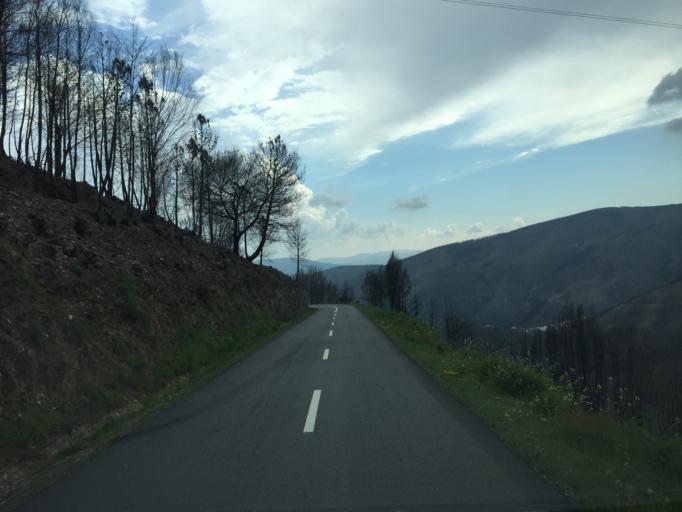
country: PT
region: Coimbra
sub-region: Arganil
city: Arganil
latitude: 40.1816
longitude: -7.9720
